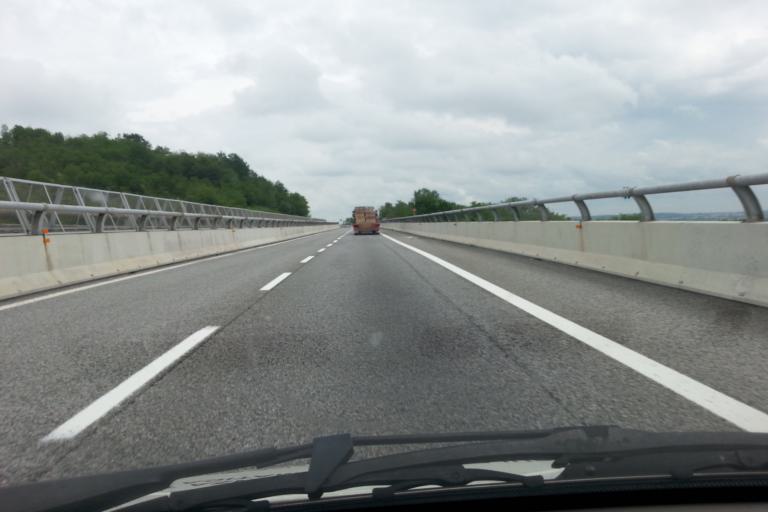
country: IT
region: Piedmont
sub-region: Provincia di Cuneo
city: Bastia Mondovi
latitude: 44.4191
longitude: 7.8916
